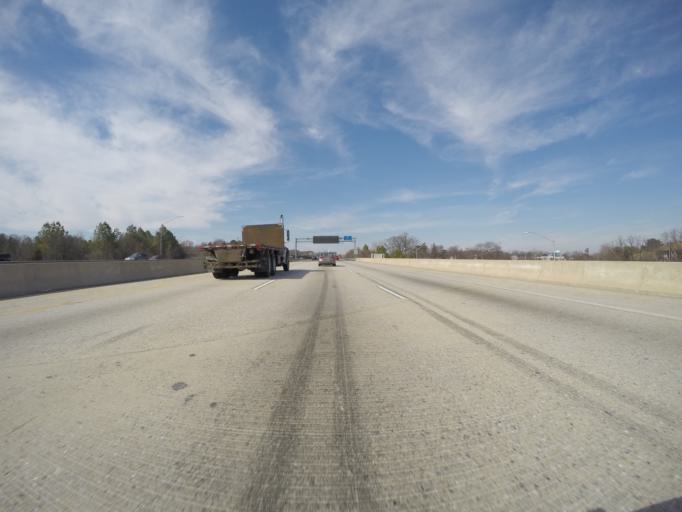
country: US
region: Maryland
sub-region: Anne Arundel County
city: South Gate
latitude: 39.1263
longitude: -76.6405
